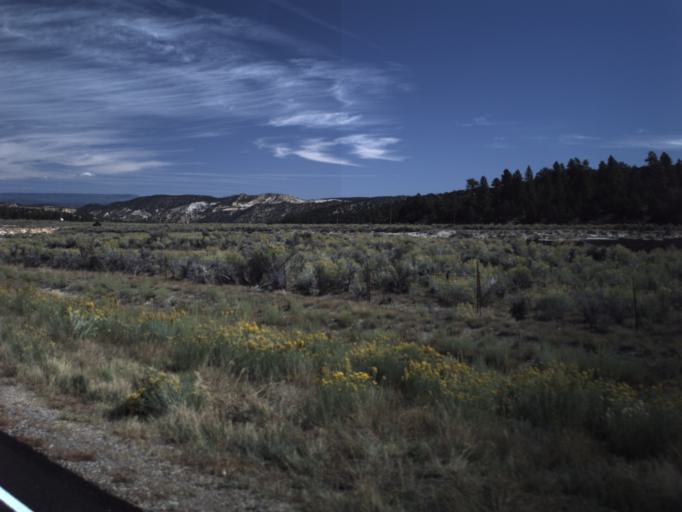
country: US
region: Utah
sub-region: Garfield County
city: Panguitch
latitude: 37.6697
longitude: -111.8297
